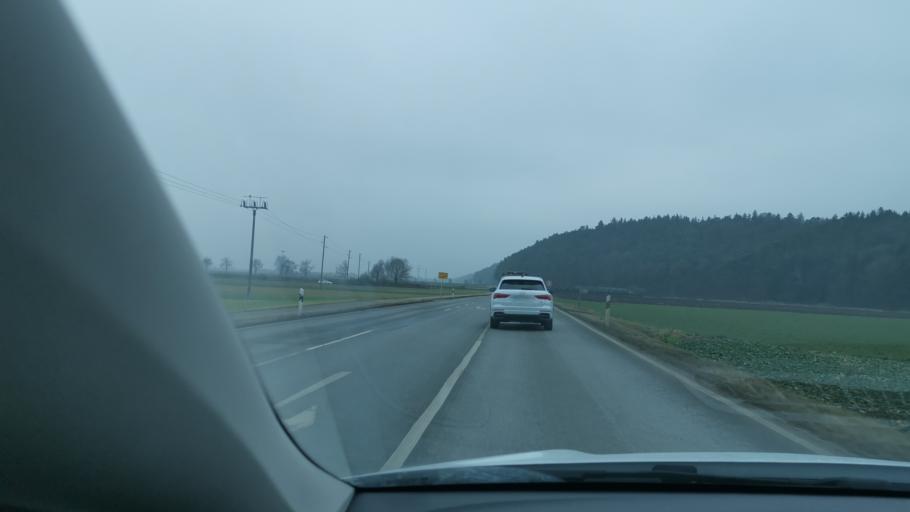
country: DE
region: Bavaria
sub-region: Swabia
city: Todtenweis
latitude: 48.5174
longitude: 10.9170
